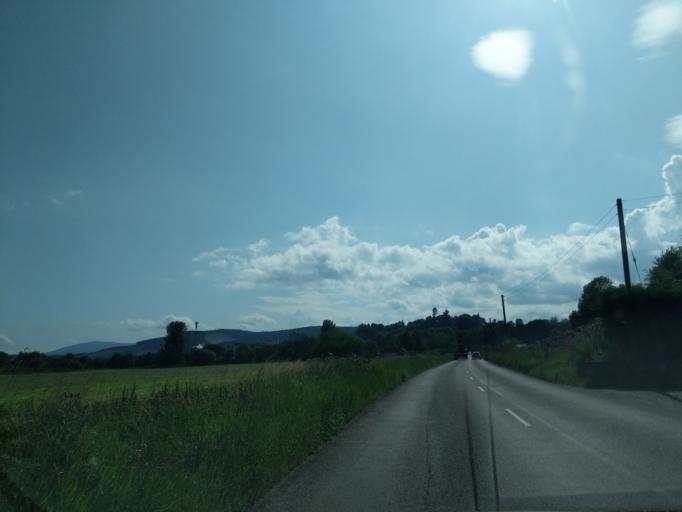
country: GB
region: Scotland
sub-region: Moray
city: Rothes
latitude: 57.5371
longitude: -3.2036
